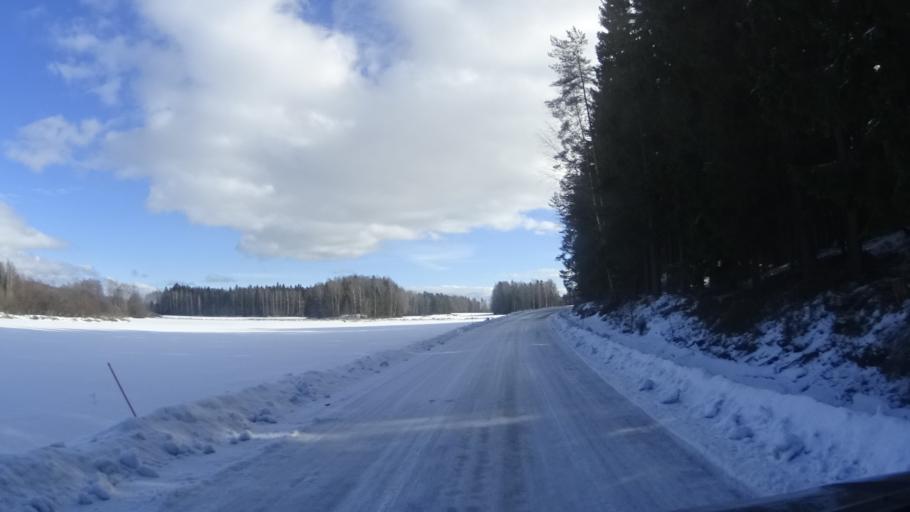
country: FI
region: Uusimaa
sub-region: Helsinki
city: Vantaa
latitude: 60.2443
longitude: 25.1757
